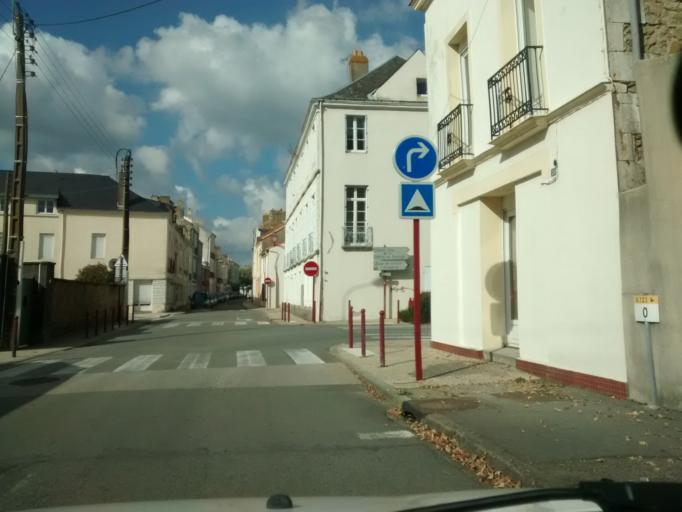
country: FR
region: Pays de la Loire
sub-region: Departement de la Loire-Atlantique
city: Saint-Paimboeuf
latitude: 47.2886
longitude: -2.0268
